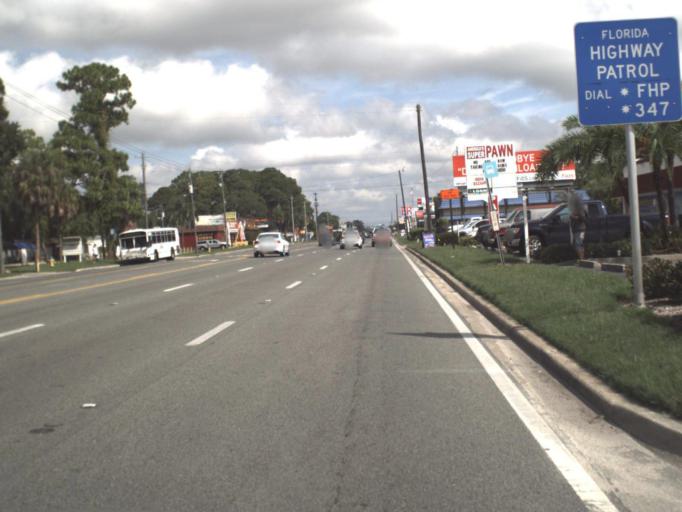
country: US
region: Florida
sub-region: Manatee County
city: South Bradenton
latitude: 27.4488
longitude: -82.5753
